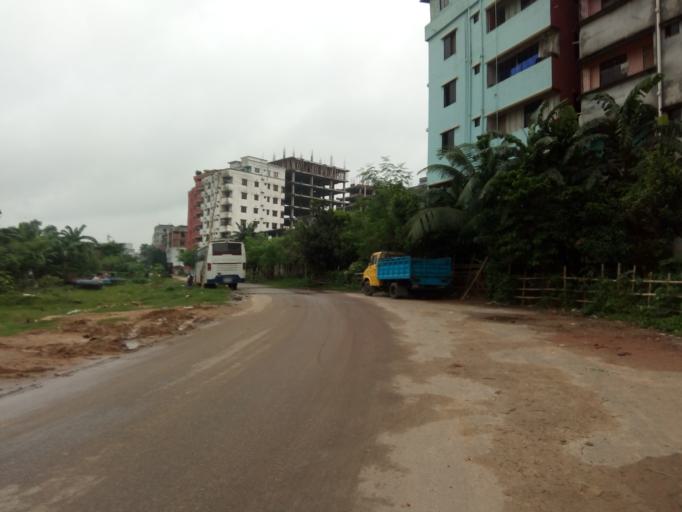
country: BD
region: Dhaka
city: Tungi
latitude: 23.8507
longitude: 90.4155
